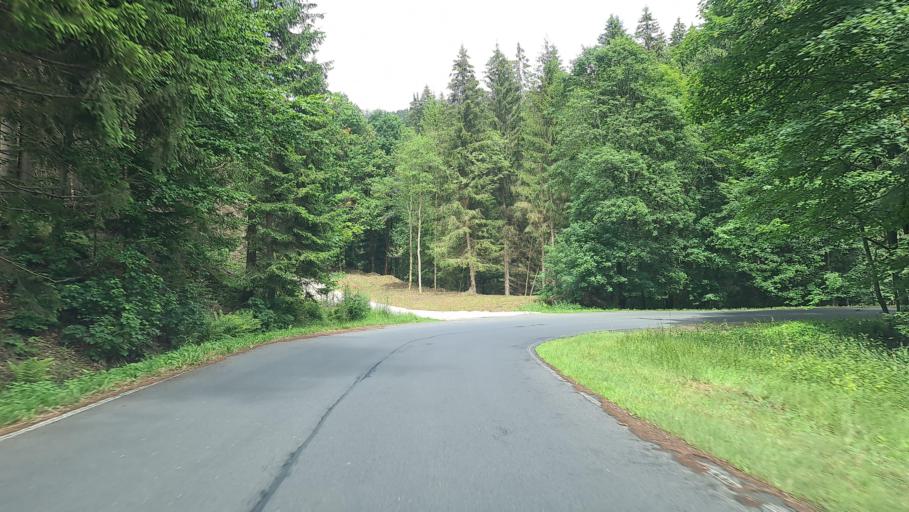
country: CZ
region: Karlovarsky
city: Kraslice
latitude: 50.3800
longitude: 12.5173
